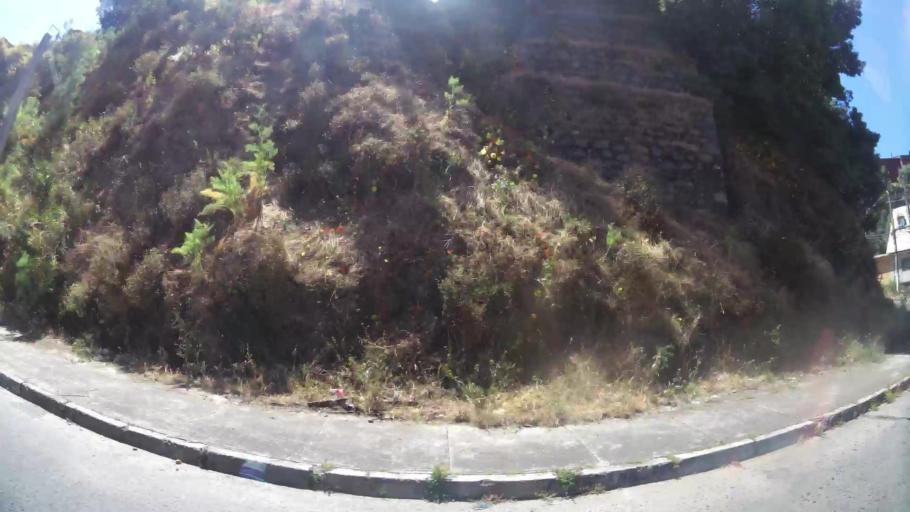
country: CL
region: Valparaiso
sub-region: Provincia de Valparaiso
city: Valparaiso
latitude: -33.0327
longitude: -71.6346
